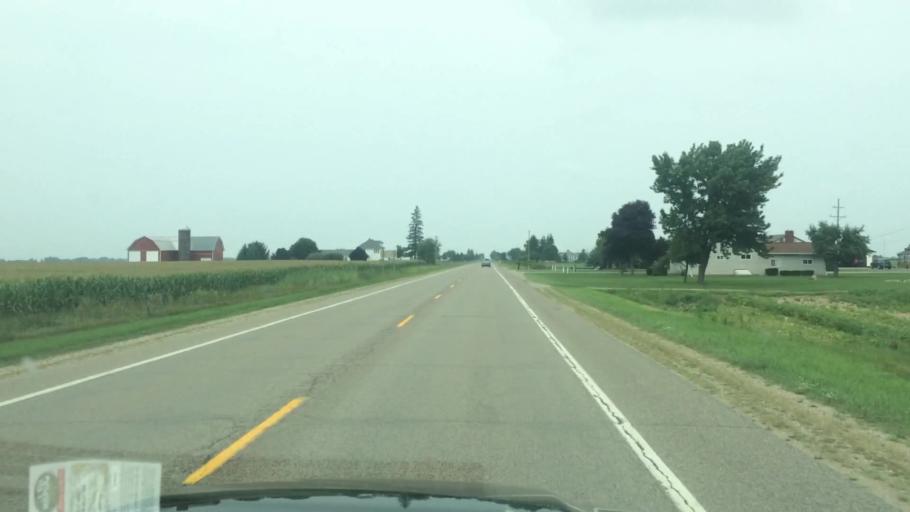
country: US
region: Michigan
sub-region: Huron County
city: Bad Axe
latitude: 43.9110
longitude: -83.0040
